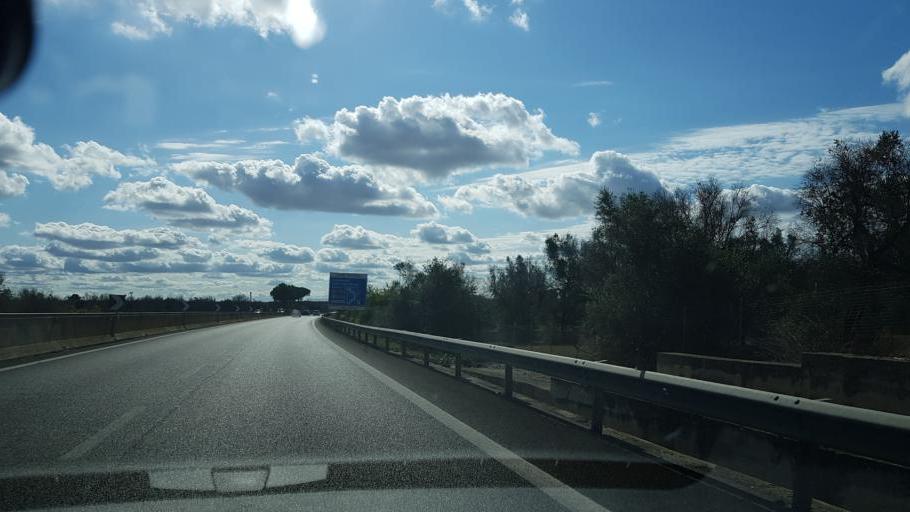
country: IT
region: Apulia
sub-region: Provincia di Lecce
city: Squinzano
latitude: 40.4452
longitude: 18.0736
